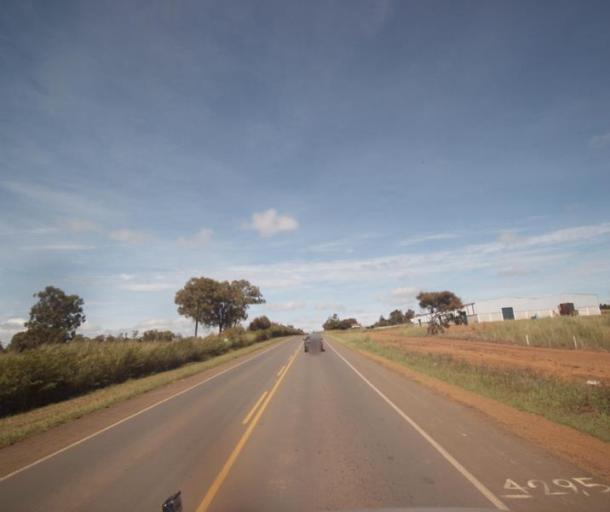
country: BR
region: Goias
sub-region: Anapolis
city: Anapolis
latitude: -16.2052
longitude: -48.9130
